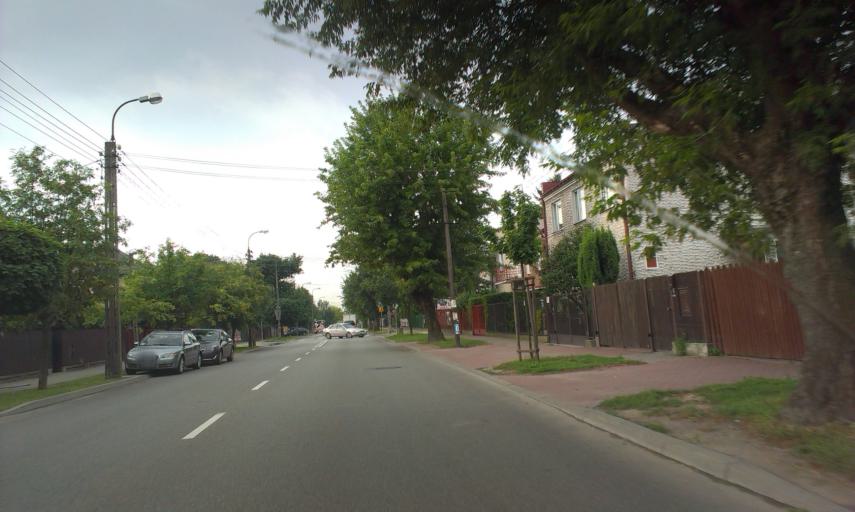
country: PL
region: Masovian Voivodeship
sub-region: Warszawa
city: Ursus
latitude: 52.1854
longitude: 20.8849
